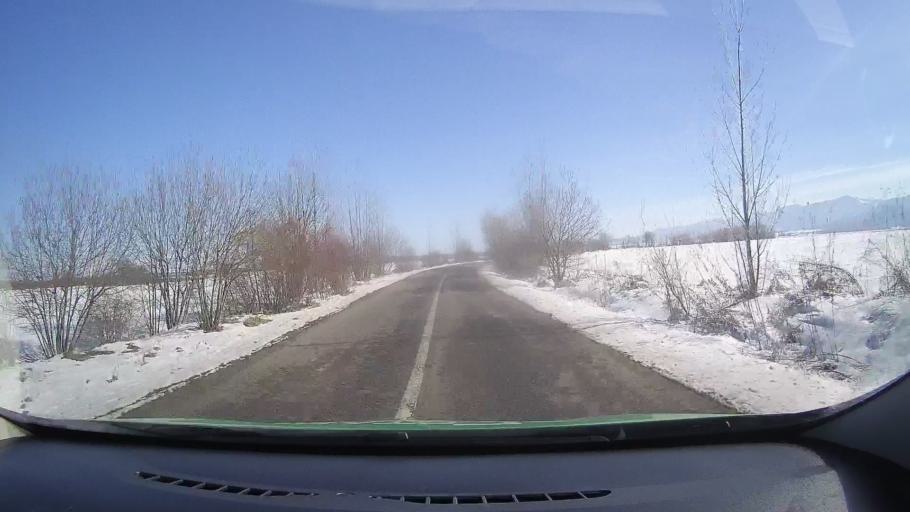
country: RO
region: Brasov
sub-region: Comuna Harseni
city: Harseni
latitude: 45.7290
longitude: 24.9795
